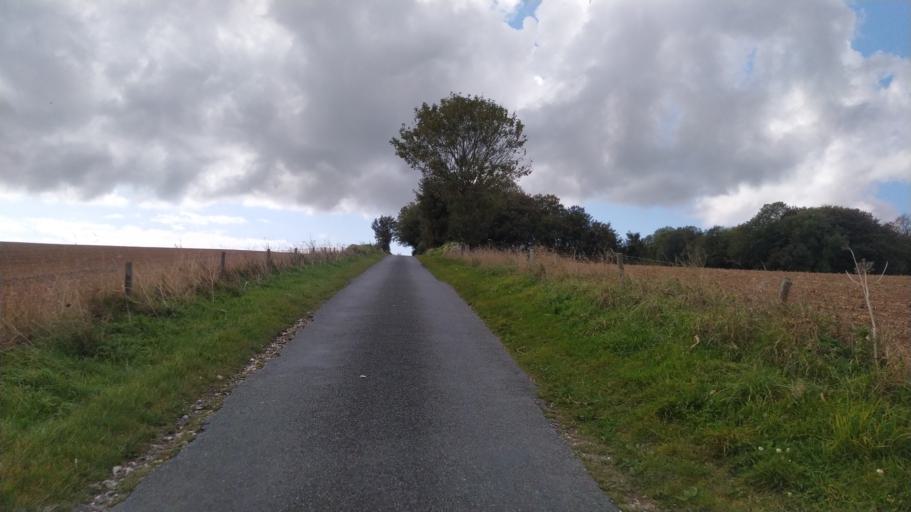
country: GB
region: England
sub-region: Dorset
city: Overcombe
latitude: 50.6705
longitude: -2.4236
